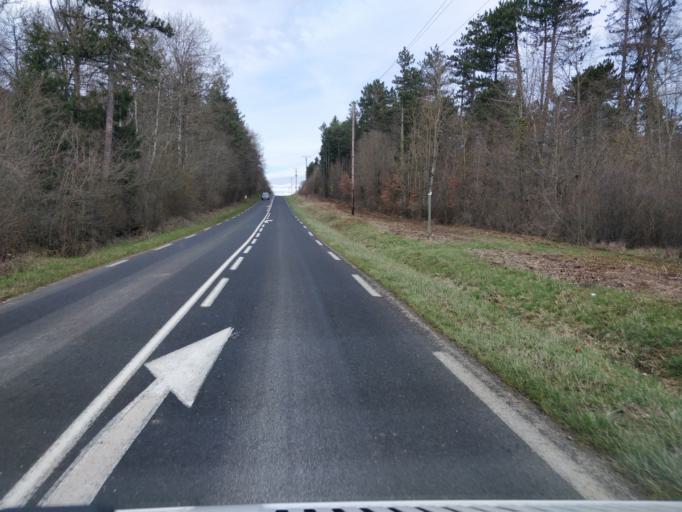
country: FR
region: Lorraine
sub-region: Departement de Meurthe-et-Moselle
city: Montauville
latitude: 48.9150
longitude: 5.9214
